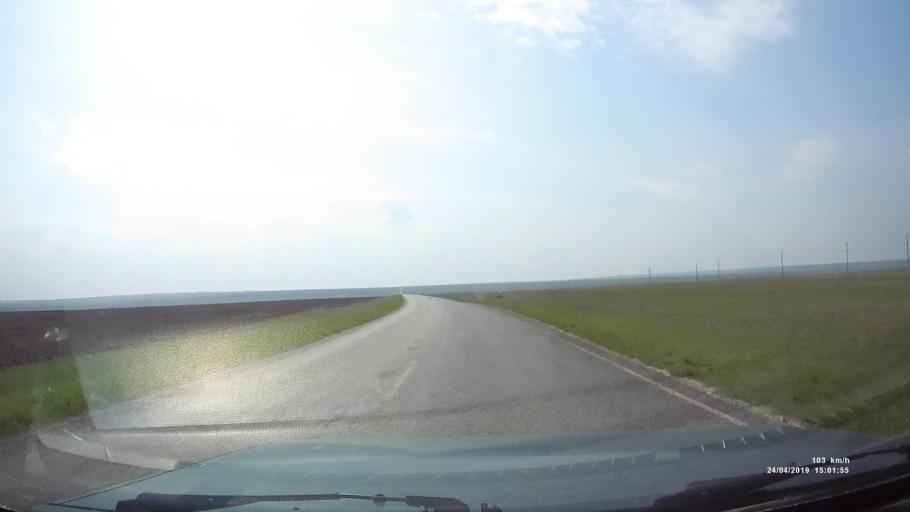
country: RU
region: Rostov
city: Remontnoye
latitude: 46.5666
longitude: 43.5233
